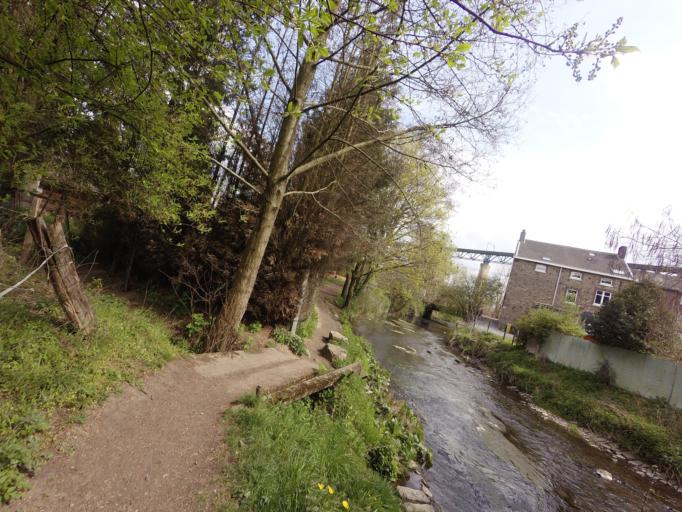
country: BE
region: Wallonia
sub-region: Province de Liege
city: La Calamine
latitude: 50.7209
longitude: 5.9859
